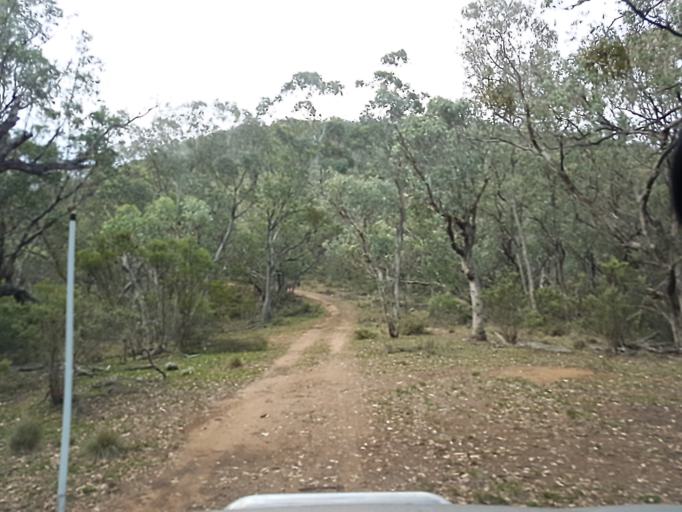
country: AU
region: New South Wales
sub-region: Snowy River
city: Jindabyne
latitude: -36.9933
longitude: 148.4090
